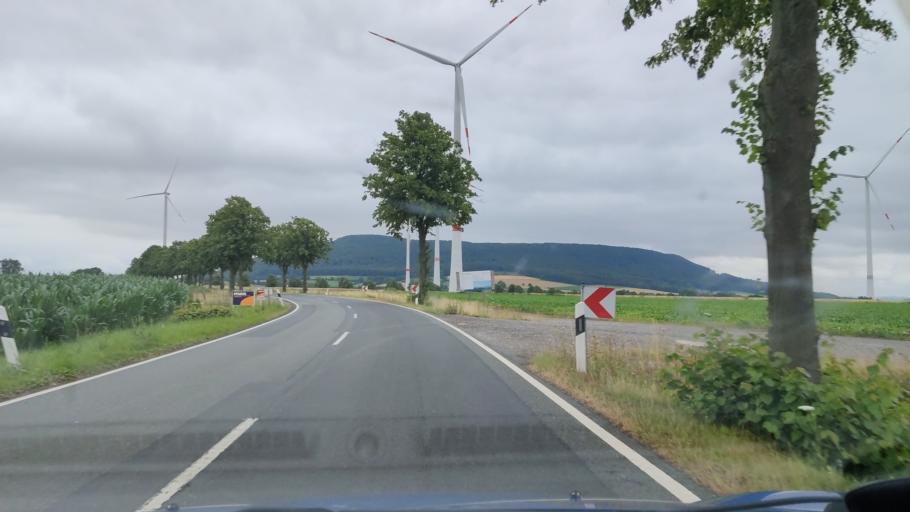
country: DE
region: Lower Saxony
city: Coppenbrugge
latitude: 52.1258
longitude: 9.4997
